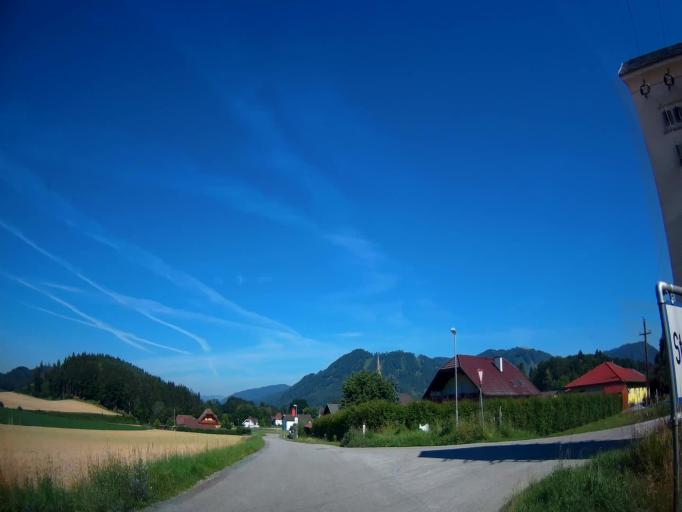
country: AT
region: Carinthia
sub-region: Politischer Bezirk Klagenfurt Land
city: Poggersdorf
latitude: 46.6790
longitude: 14.5070
